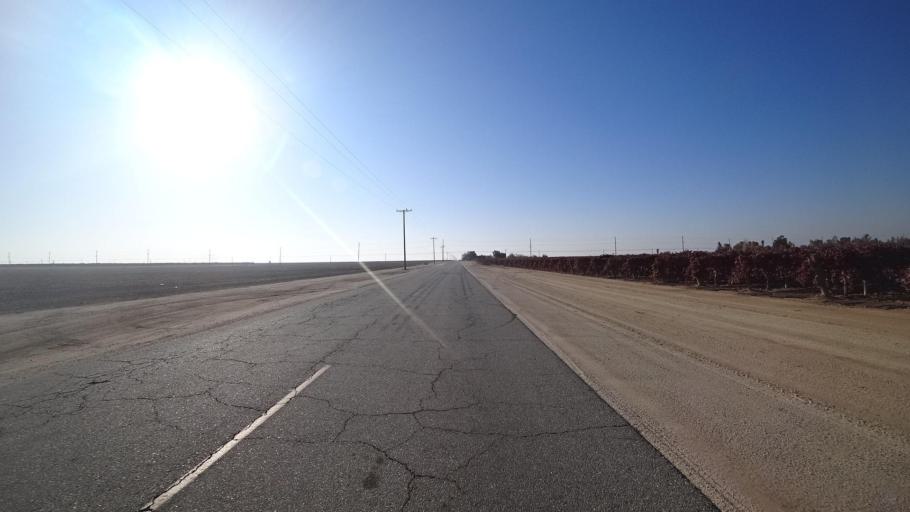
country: US
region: California
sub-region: Tulare County
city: Richgrove
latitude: 35.7787
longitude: -119.1692
